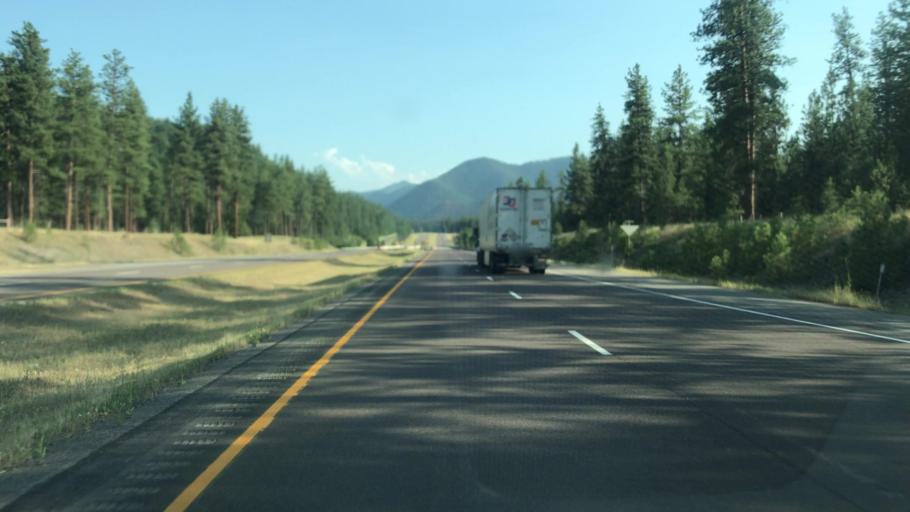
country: US
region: Montana
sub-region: Mineral County
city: Superior
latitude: 47.0722
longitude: -114.7655
